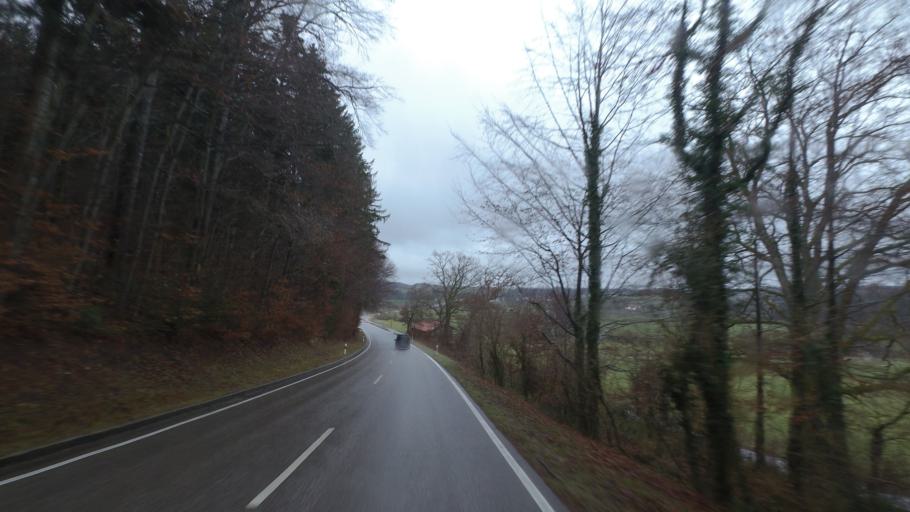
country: DE
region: Bavaria
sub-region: Upper Bavaria
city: Sankt Leonhard am Wonneberg
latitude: 47.9334
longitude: 12.7012
